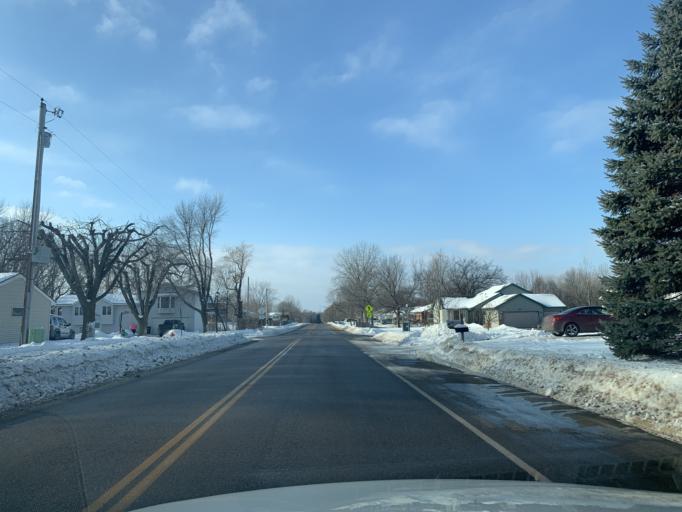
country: US
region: Minnesota
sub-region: Wright County
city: Buffalo
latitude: 45.1943
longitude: -93.8359
